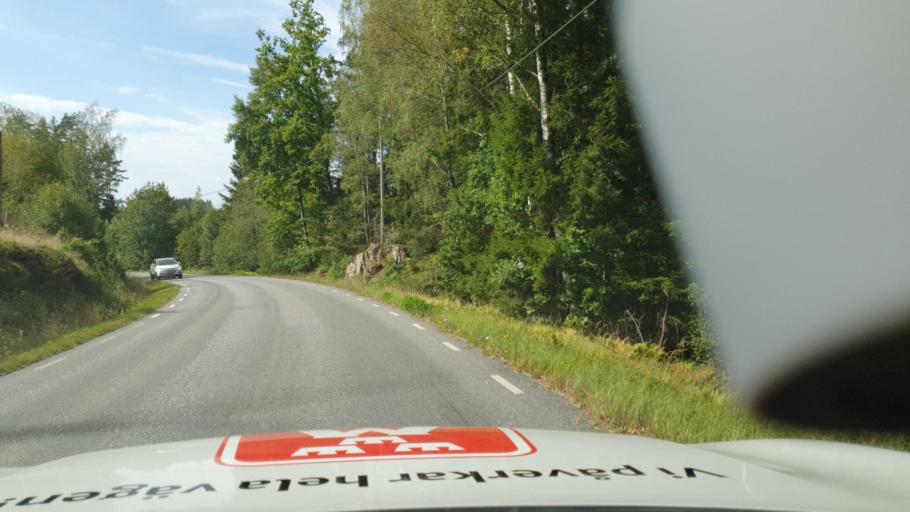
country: SE
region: Vaestra Goetaland
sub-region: Marks Kommun
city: Kinna
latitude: 57.3891
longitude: 12.7161
